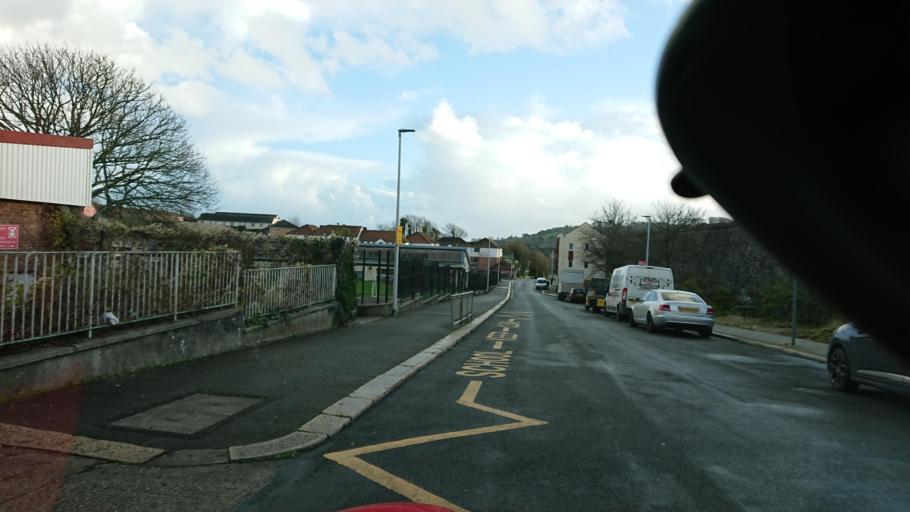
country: GB
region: England
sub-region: Cornwall
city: Millbrook
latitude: 50.3680
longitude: -4.1777
